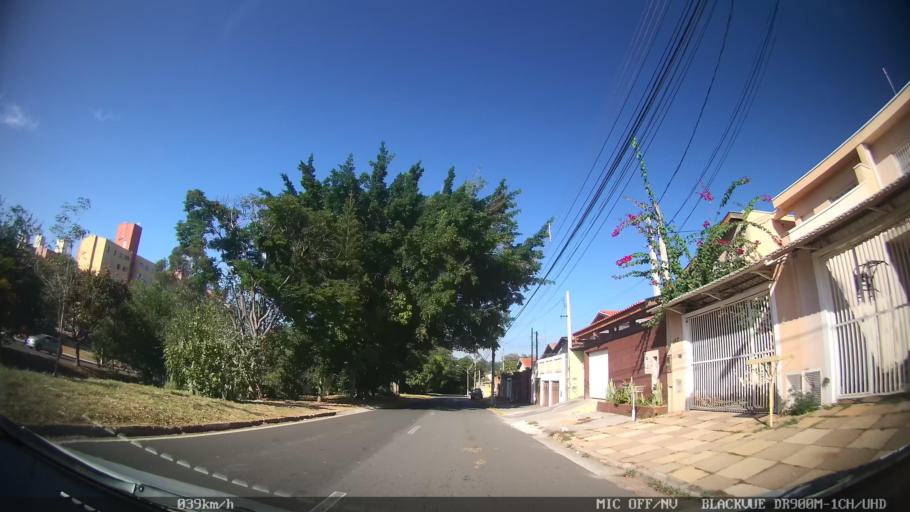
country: BR
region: Sao Paulo
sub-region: Campinas
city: Campinas
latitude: -22.9489
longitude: -47.0974
